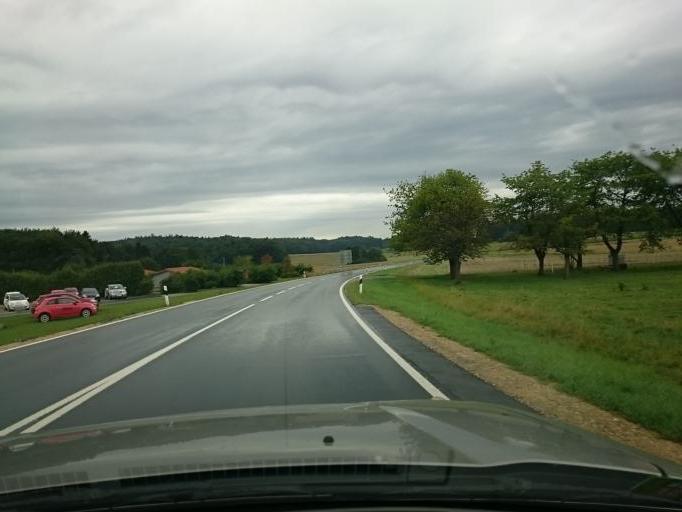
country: DE
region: Bavaria
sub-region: Upper Franconia
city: Obertrubach
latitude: 49.6973
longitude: 11.3926
